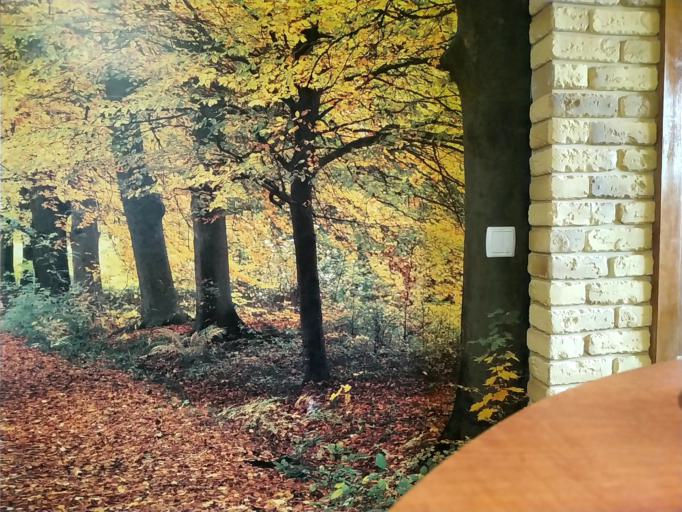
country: RU
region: Novgorod
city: Opechenskiy Posad
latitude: 58.2689
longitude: 34.0174
